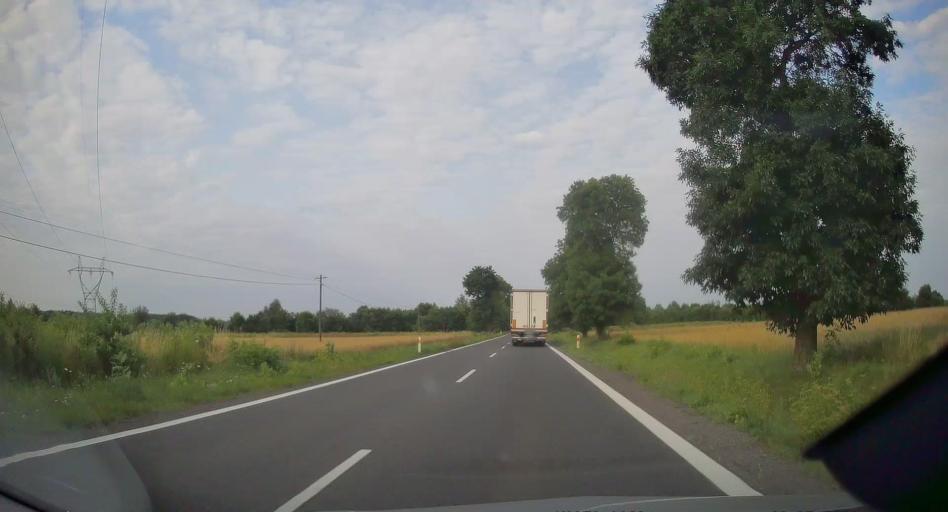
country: PL
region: Silesian Voivodeship
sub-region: Powiat czestochowski
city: Rudniki
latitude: 50.8950
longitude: 19.2763
